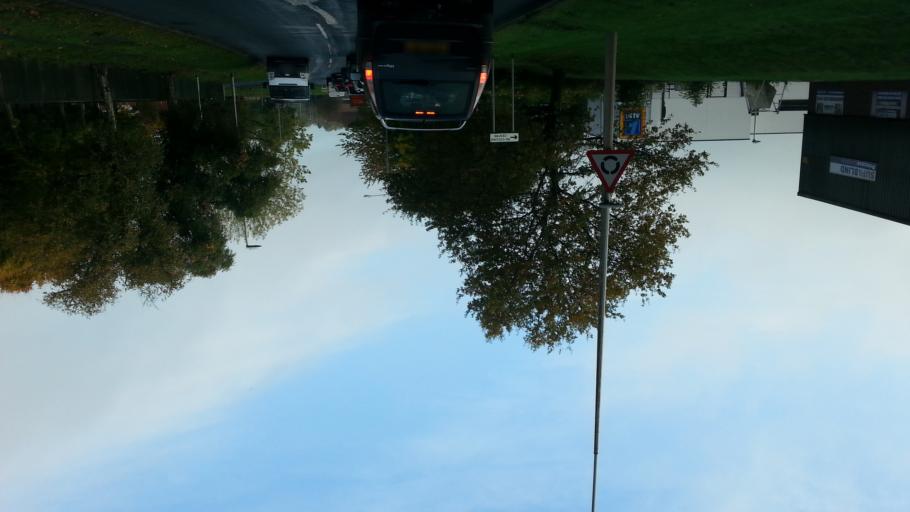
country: GB
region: England
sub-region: Worcestershire
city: Bromsgrove
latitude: 52.3192
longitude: -2.0620
